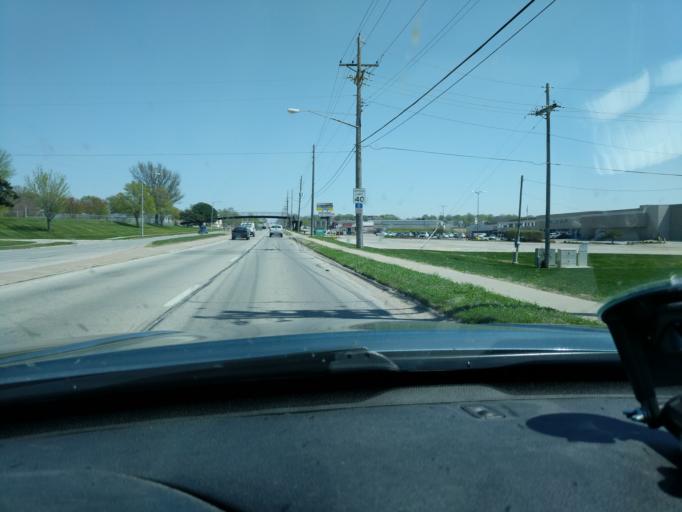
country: US
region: Nebraska
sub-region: Douglas County
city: Ralston
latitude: 41.2342
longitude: -96.0483
